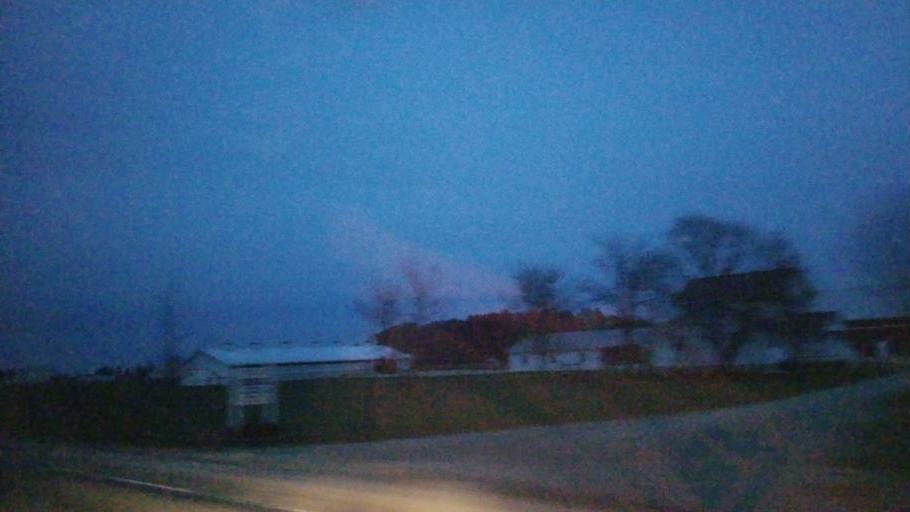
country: US
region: Indiana
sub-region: Adams County
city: Berne
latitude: 40.6880
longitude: -84.9559
